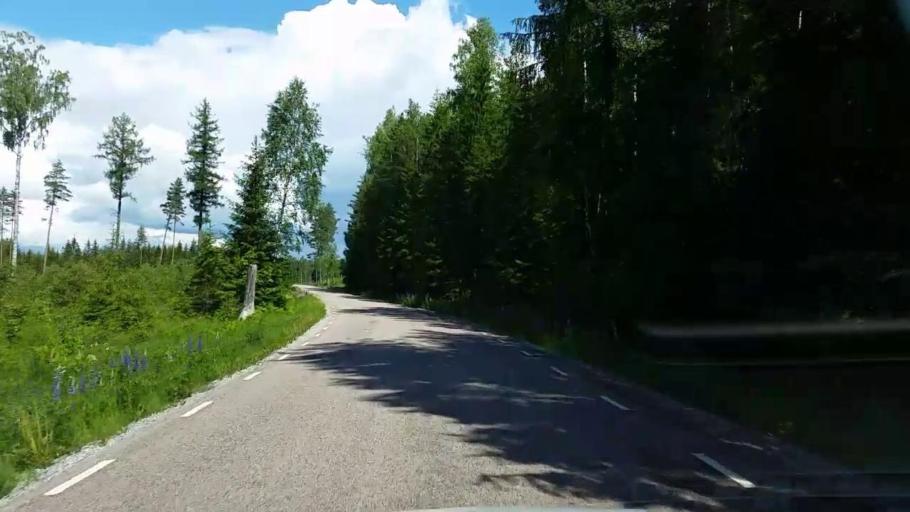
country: SE
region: Vaestmanland
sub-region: Fagersta Kommun
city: Fagersta
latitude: 59.9883
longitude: 15.7416
